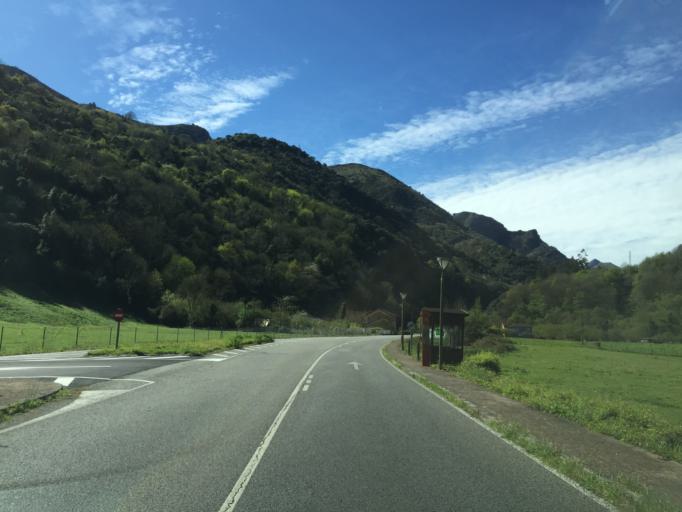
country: ES
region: Asturias
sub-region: Province of Asturias
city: Proaza
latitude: 43.2910
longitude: -5.9824
